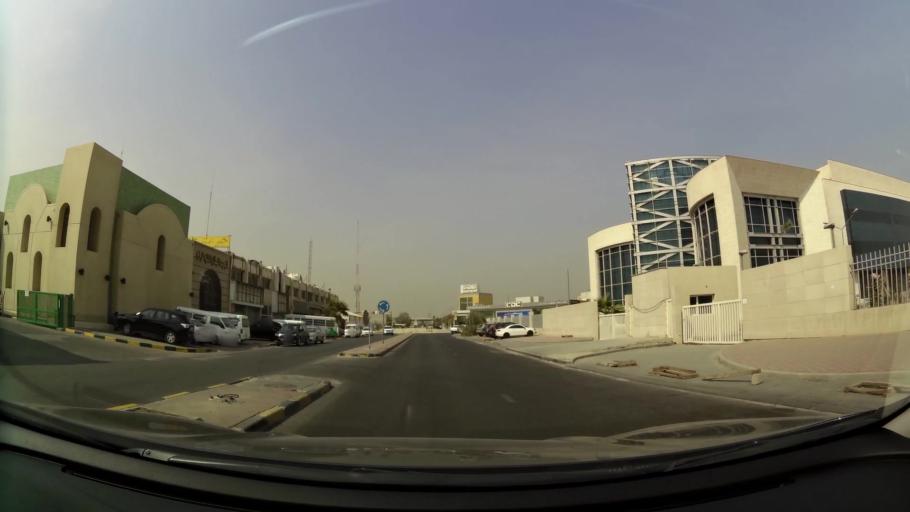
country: KW
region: Al Asimah
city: Ash Shamiyah
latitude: 29.3290
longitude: 47.9377
